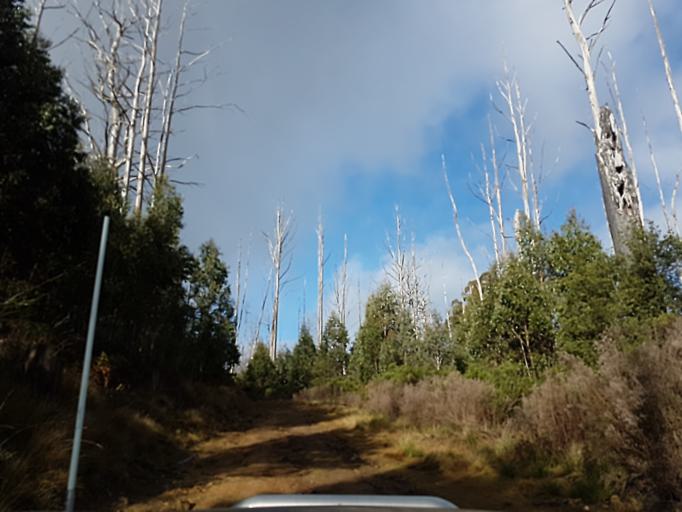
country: AU
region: Victoria
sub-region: Yarra Ranges
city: Millgrove
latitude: -37.5375
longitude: 145.8135
